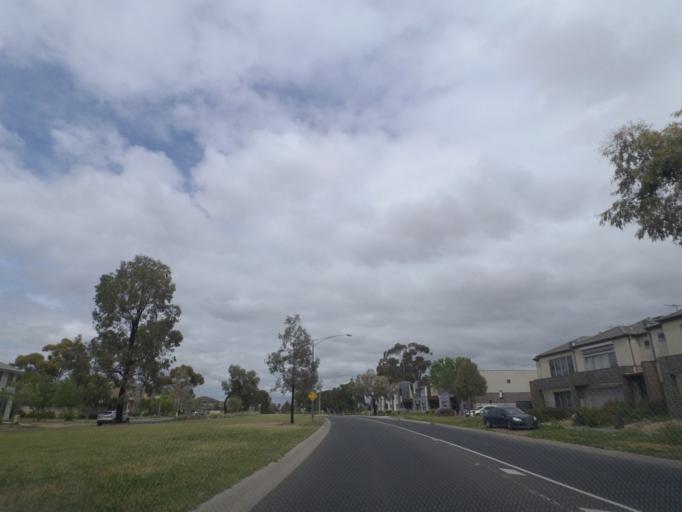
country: AU
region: Victoria
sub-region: Brimbank
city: Cairnlea
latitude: -37.7597
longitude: 144.7904
